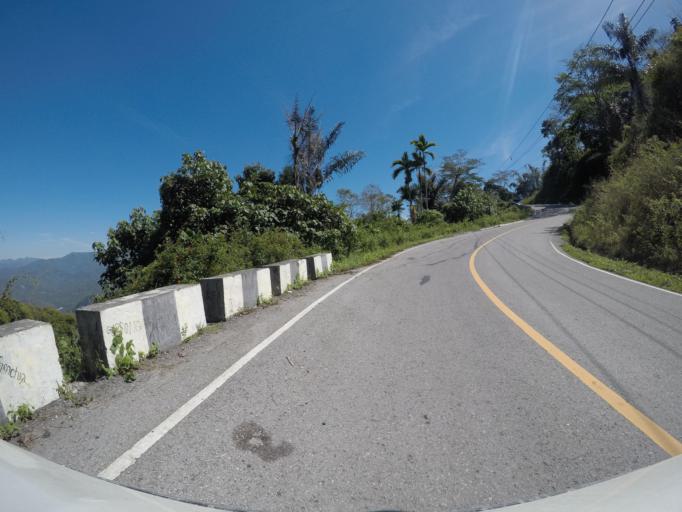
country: TL
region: Manufahi
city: Same
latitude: -8.9017
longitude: 125.9769
